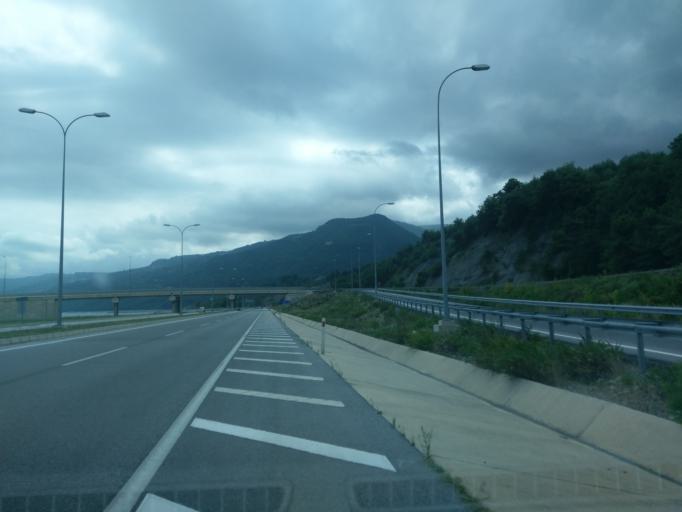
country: TR
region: Sinop
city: Dikmen
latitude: 41.7281
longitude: 35.2633
